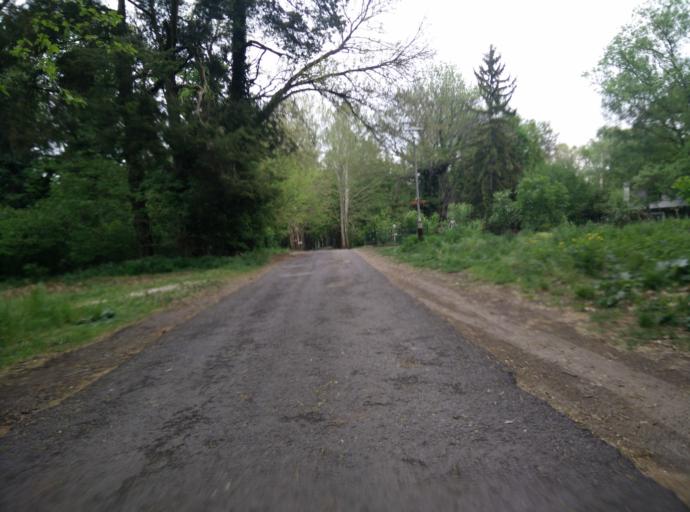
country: HU
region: Pest
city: Fot
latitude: 47.6054
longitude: 19.1901
